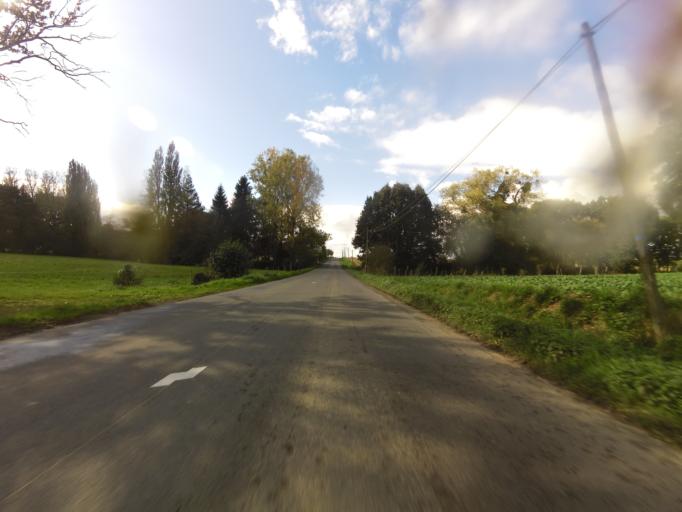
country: FR
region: Brittany
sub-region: Departement d'Ille-et-Vilaine
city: Erce-pres-Liffre
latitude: 48.2555
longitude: -1.5358
